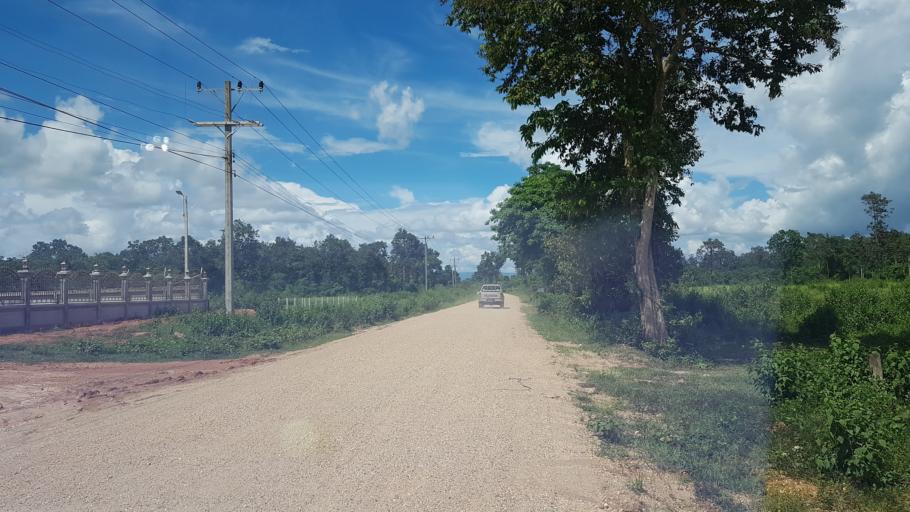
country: LA
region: Vientiane
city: Vientiane
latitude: 18.2262
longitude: 102.5212
